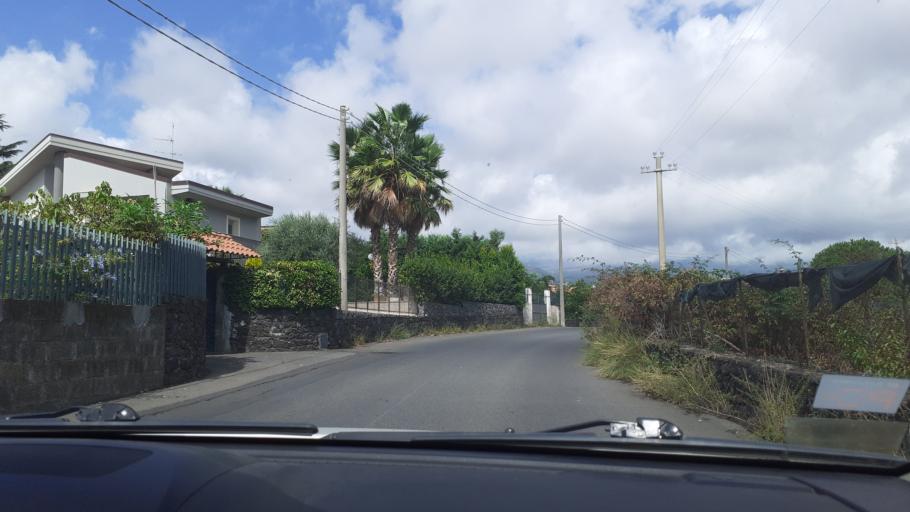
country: IT
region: Sicily
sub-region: Catania
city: Trecastagni
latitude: 37.6006
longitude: 15.0730
